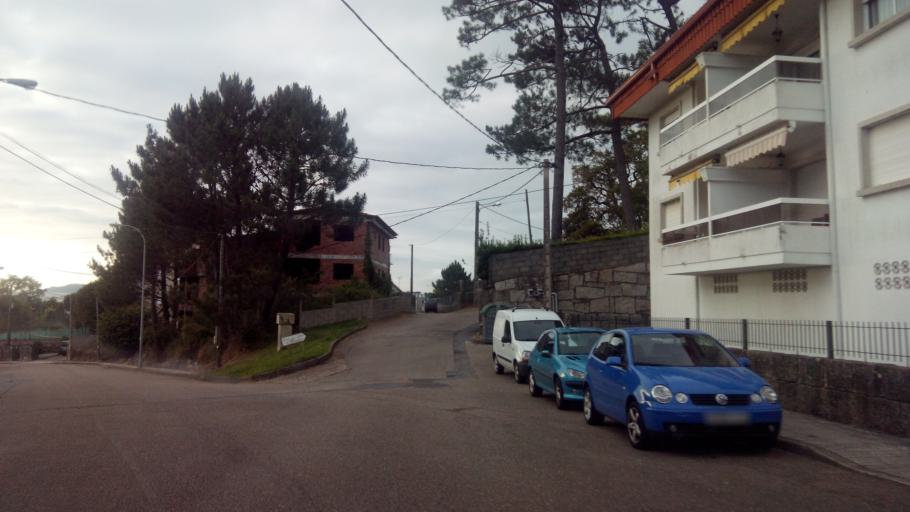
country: ES
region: Galicia
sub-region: Provincia de Pontevedra
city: Nigran
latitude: 42.1242
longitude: -8.8172
